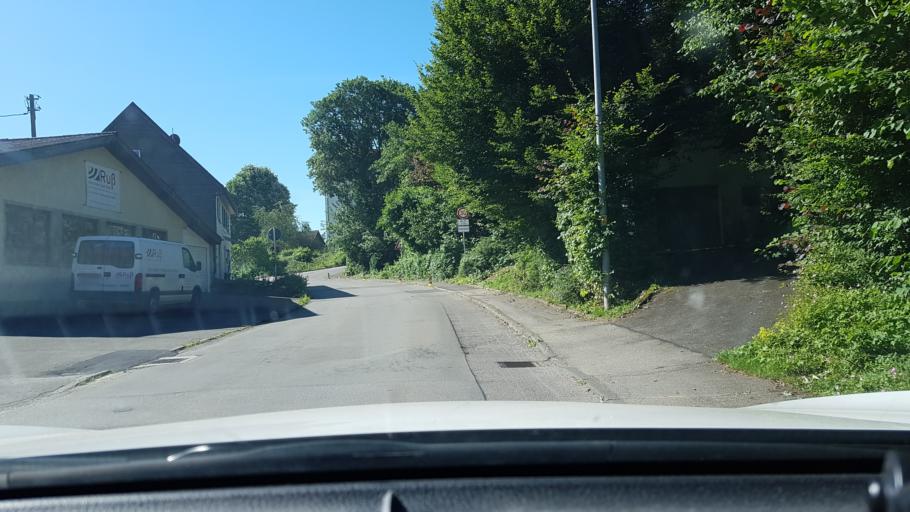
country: DE
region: Baden-Wuerttemberg
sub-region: Tuebingen Region
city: Gutenzell-Hurbel
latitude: 48.1091
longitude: 9.9480
